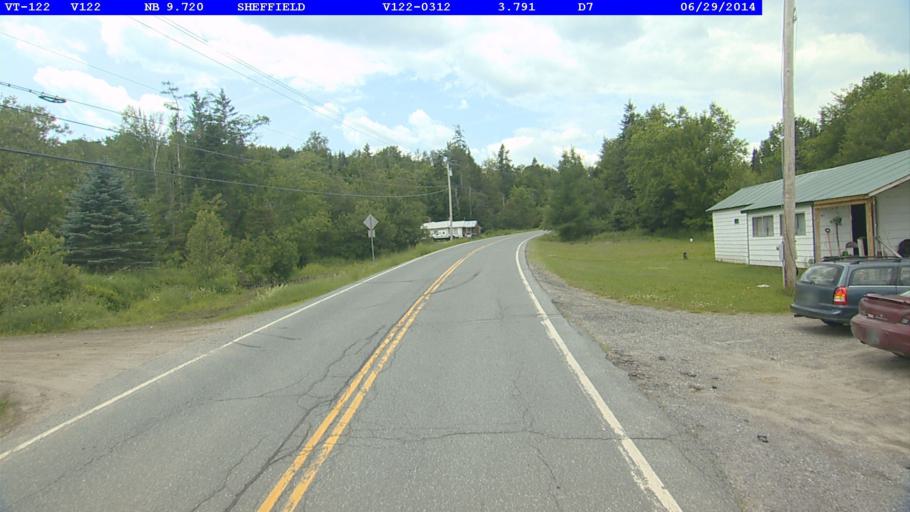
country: US
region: Vermont
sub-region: Caledonia County
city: Lyndonville
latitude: 44.6307
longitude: -72.1365
